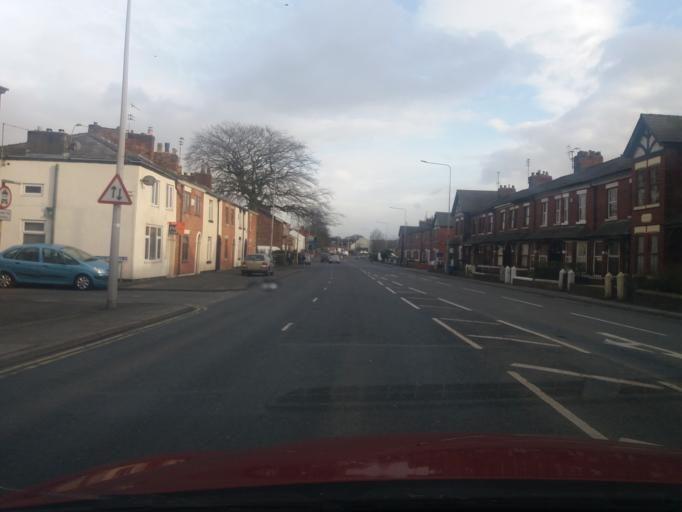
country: GB
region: England
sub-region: Lancashire
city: Preston
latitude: 53.7517
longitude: -2.6782
